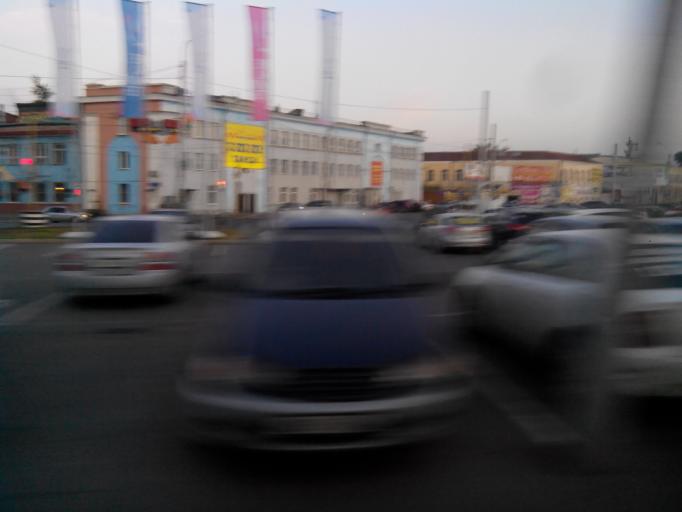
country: RU
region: Krasnoyarskiy
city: Krasnoyarsk
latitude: 56.0063
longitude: 92.8328
